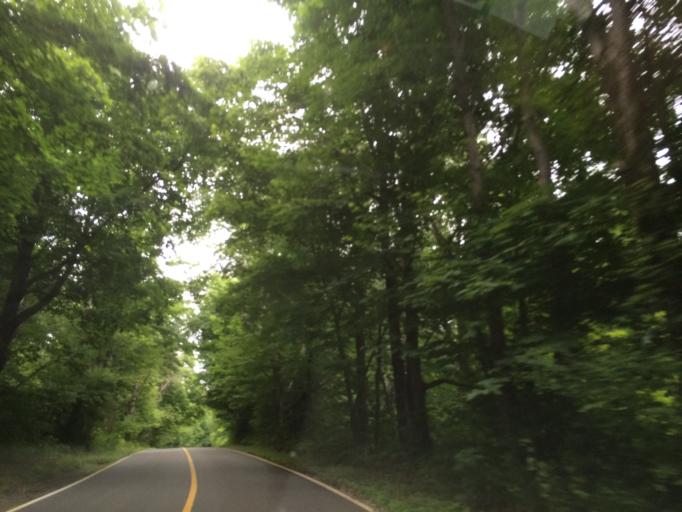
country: US
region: Massachusetts
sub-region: Berkshire County
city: Lanesborough
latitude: 42.5632
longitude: -73.2098
